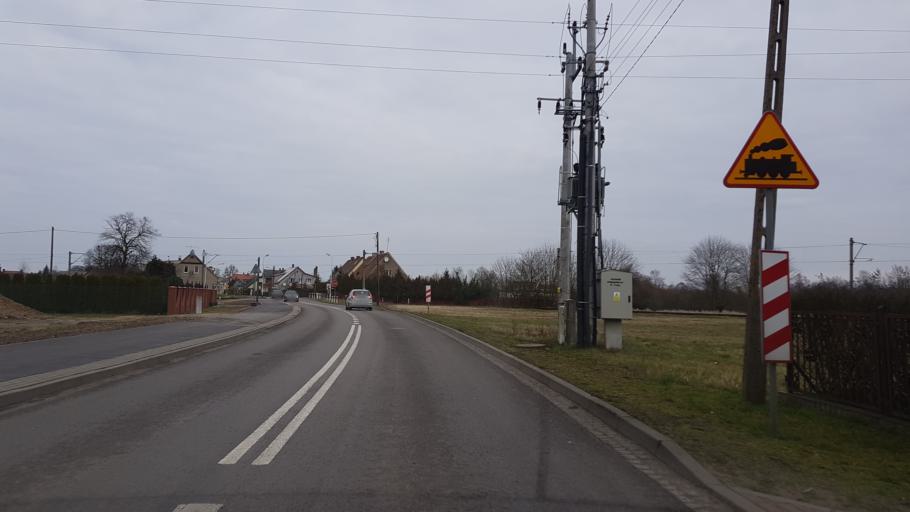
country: PL
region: West Pomeranian Voivodeship
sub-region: Powiat goleniowski
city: Stepnica
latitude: 53.6500
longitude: 14.5100
